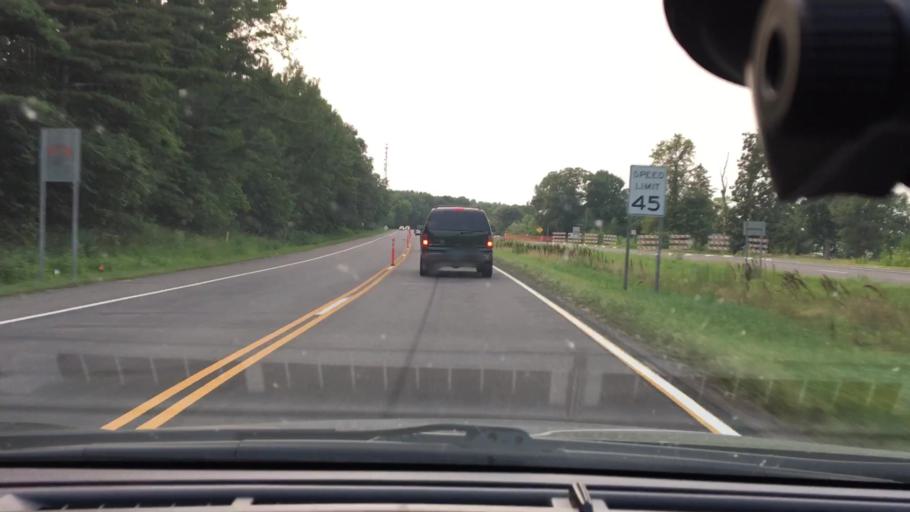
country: US
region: Minnesota
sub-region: Mille Lacs County
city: Vineland
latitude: 46.2851
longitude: -93.8215
